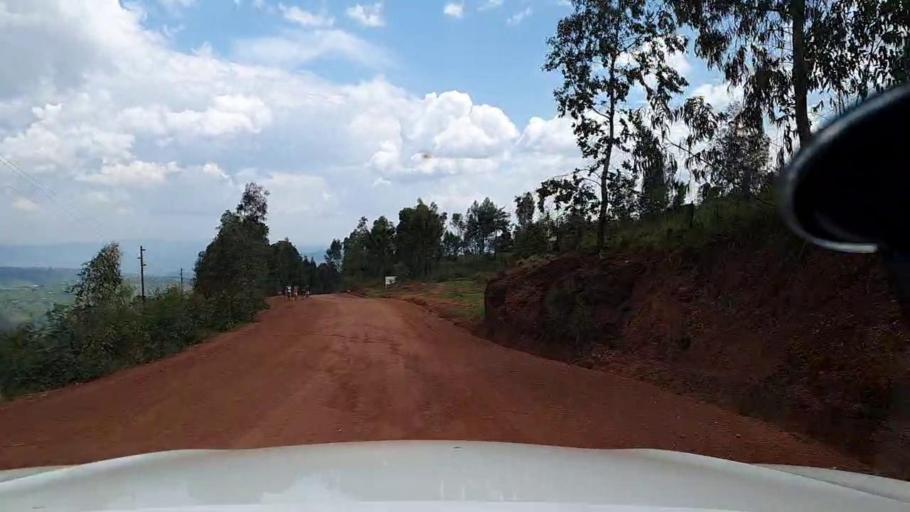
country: RW
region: Kigali
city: Kigali
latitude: -1.8131
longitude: 29.8467
